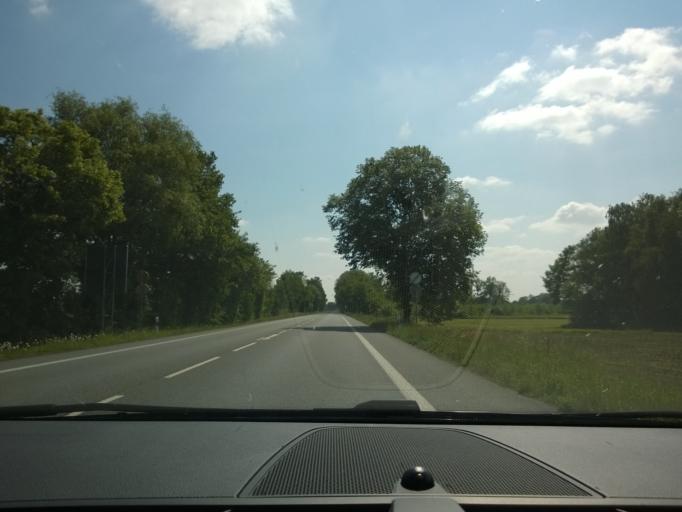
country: DE
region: North Rhine-Westphalia
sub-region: Regierungsbezirk Munster
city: Sudlohn
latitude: 51.9309
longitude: 6.8536
